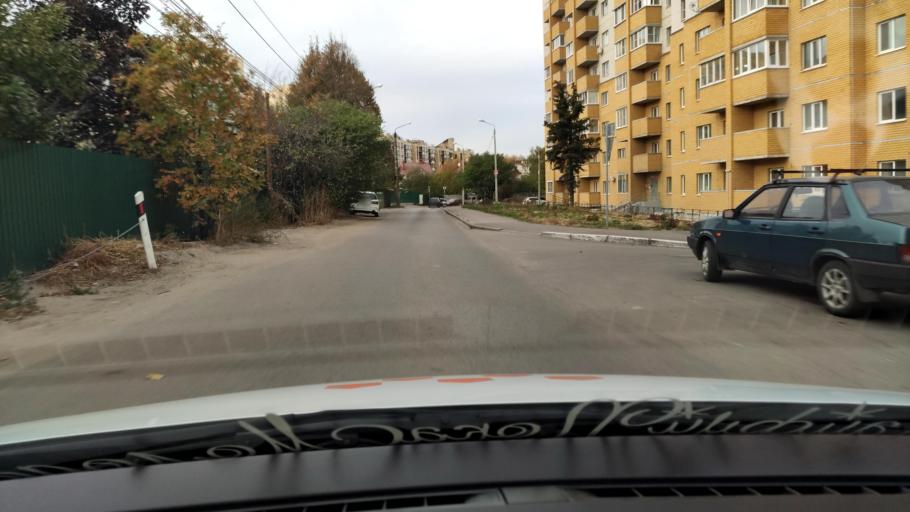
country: RU
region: Voronezj
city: Voronezh
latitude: 51.7005
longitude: 39.2037
